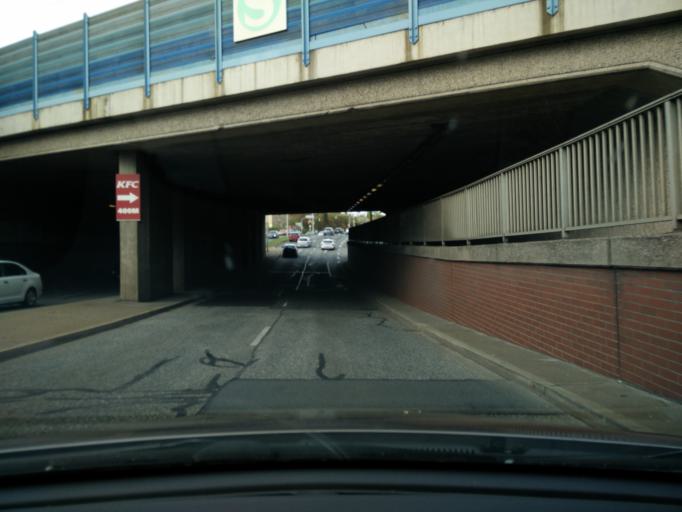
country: DE
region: Bavaria
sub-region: Regierungsbezirk Mittelfranken
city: Nuernberg
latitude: 49.4367
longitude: 11.1172
